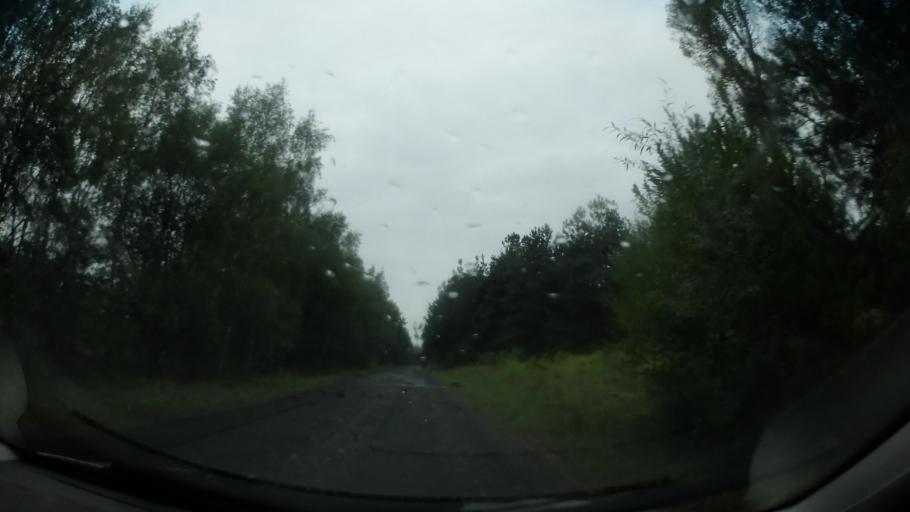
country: CZ
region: Central Bohemia
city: Milovice
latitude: 50.2430
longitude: 14.9123
